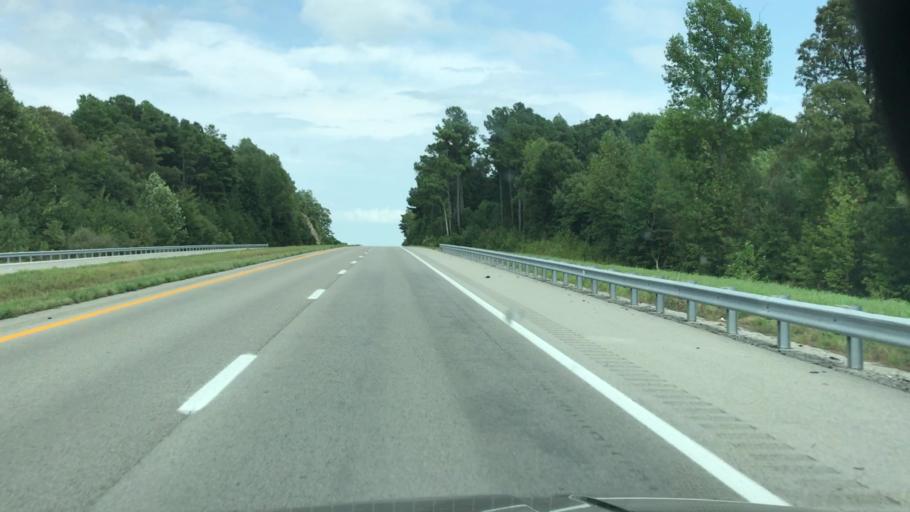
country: US
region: Kentucky
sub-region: Hopkins County
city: Earlington
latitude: 37.2006
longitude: -87.5376
